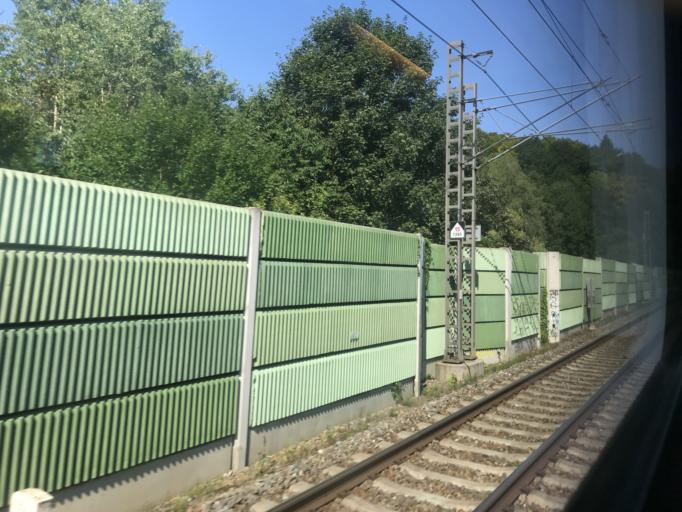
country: CZ
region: Central Bohemia
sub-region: Okres Praha-Vychod
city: Mnichovice
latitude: 49.9339
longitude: 14.7054
